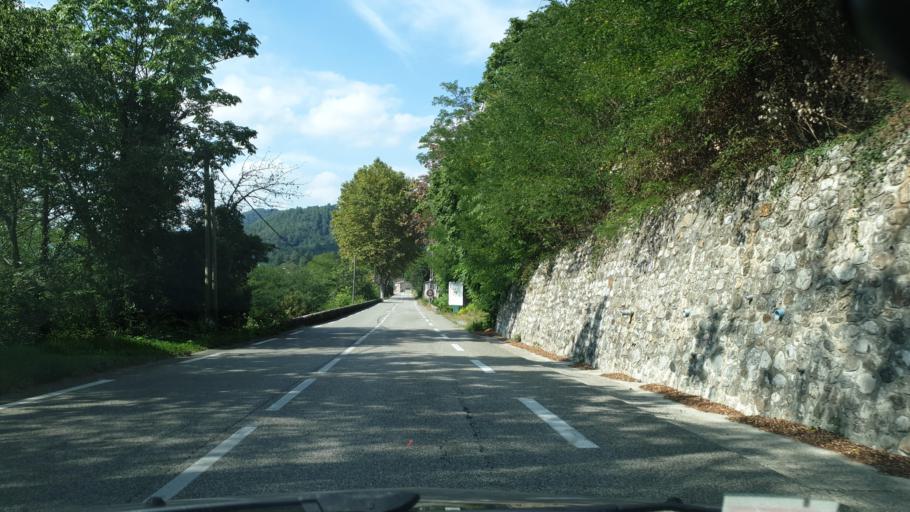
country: FR
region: Rhone-Alpes
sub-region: Departement de l'Ardeche
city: Vernoux-en-Vivarais
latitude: 44.8298
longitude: 4.6831
